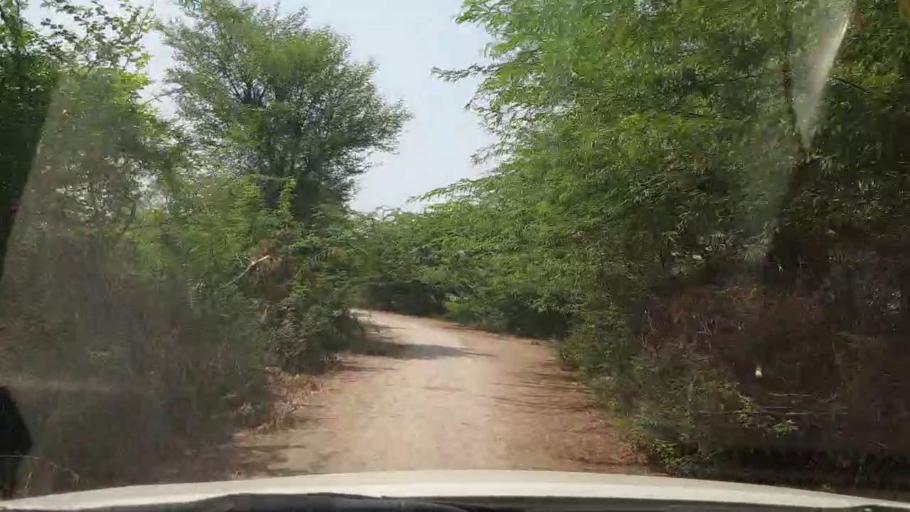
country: PK
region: Sindh
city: Shikarpur
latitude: 27.9855
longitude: 68.7166
